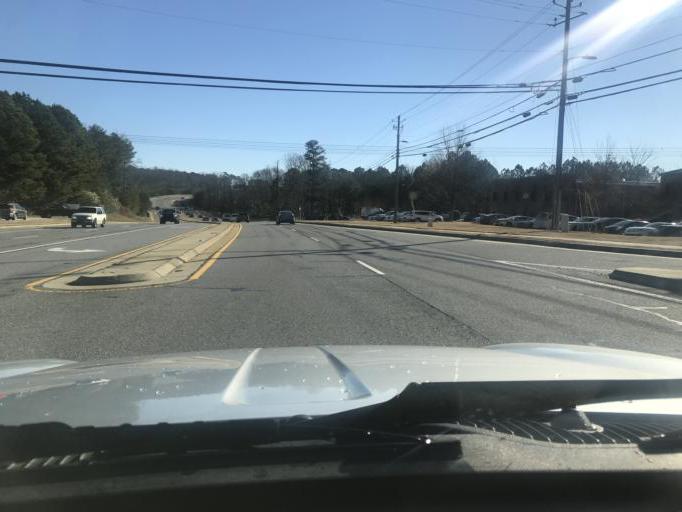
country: US
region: Georgia
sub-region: Gwinnett County
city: Suwanee
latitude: 33.9749
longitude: -84.0660
